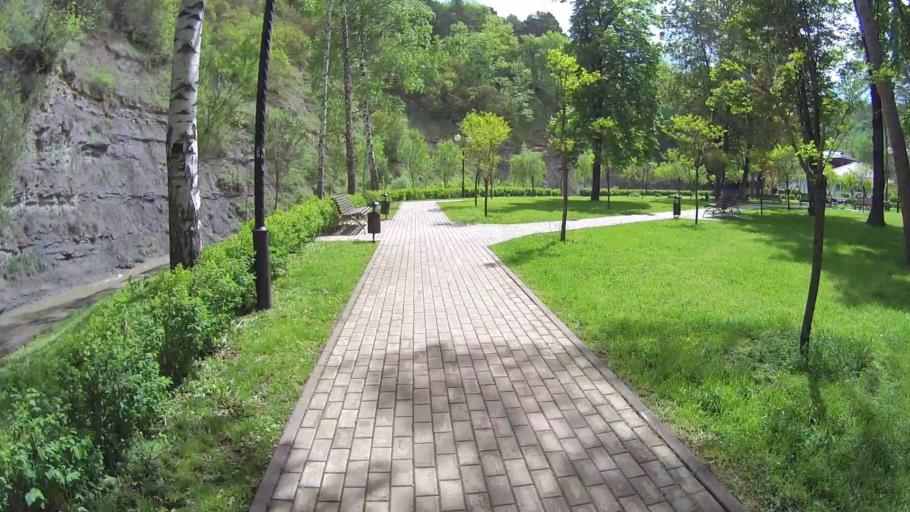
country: RU
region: Stavropol'skiy
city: Kislovodsk
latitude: 43.8922
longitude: 42.7211
